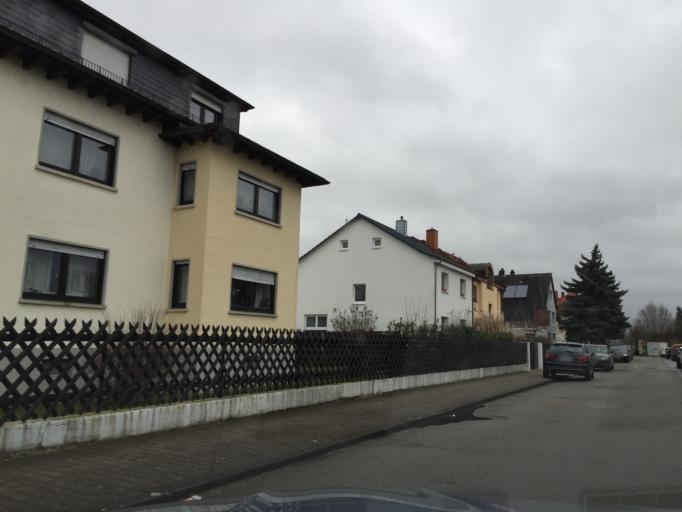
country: DE
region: Baden-Wuerttemberg
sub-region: Karlsruhe Region
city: Plankstadt
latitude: 49.3882
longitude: 8.5946
